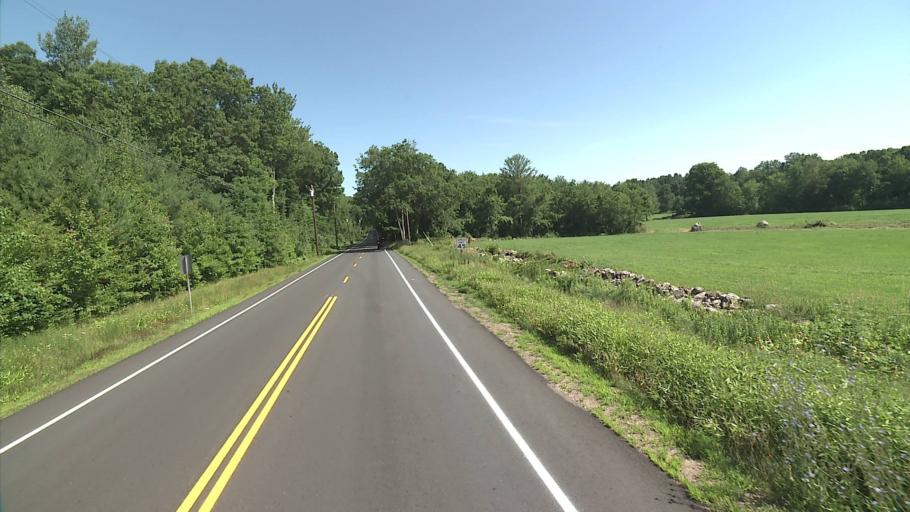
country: US
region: Connecticut
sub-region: Litchfield County
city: Northwest Harwinton
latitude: 41.7534
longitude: -73.0235
